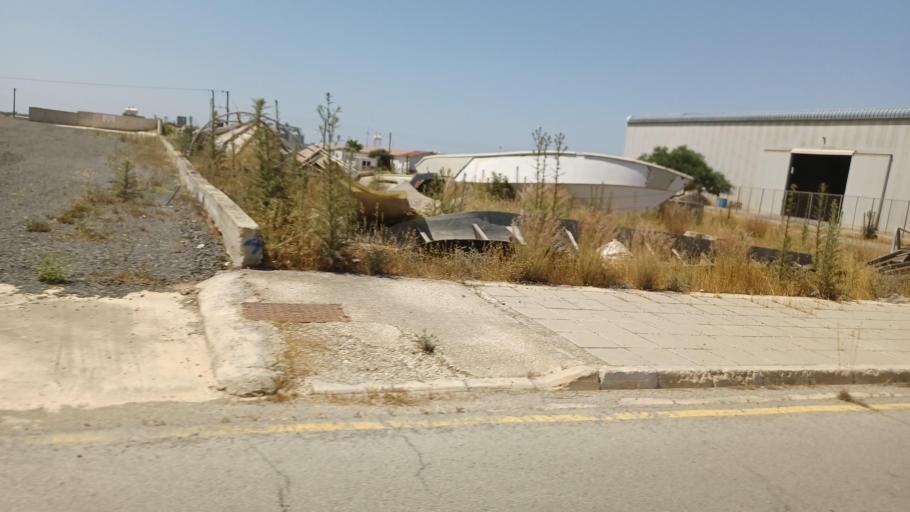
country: CY
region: Ammochostos
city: Frenaros
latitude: 35.0331
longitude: 33.9109
